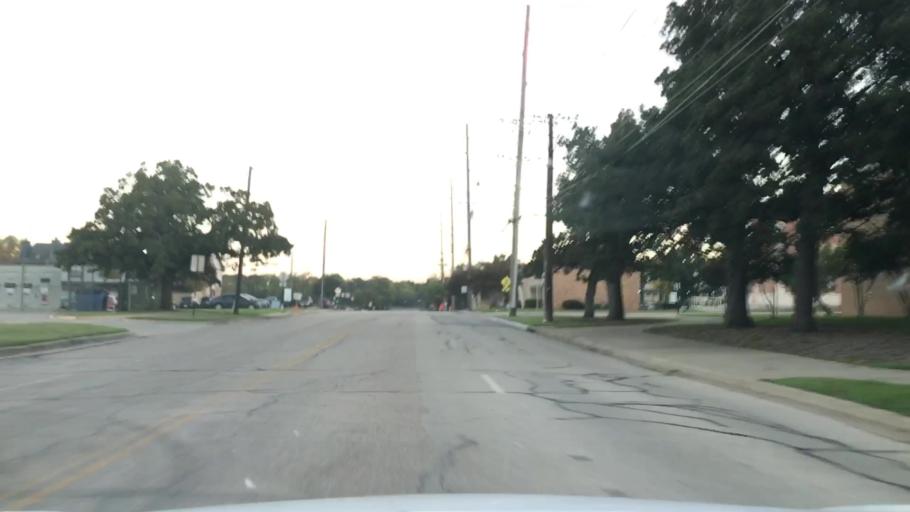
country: US
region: Texas
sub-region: Denton County
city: Denton
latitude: 33.2121
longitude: -97.1551
